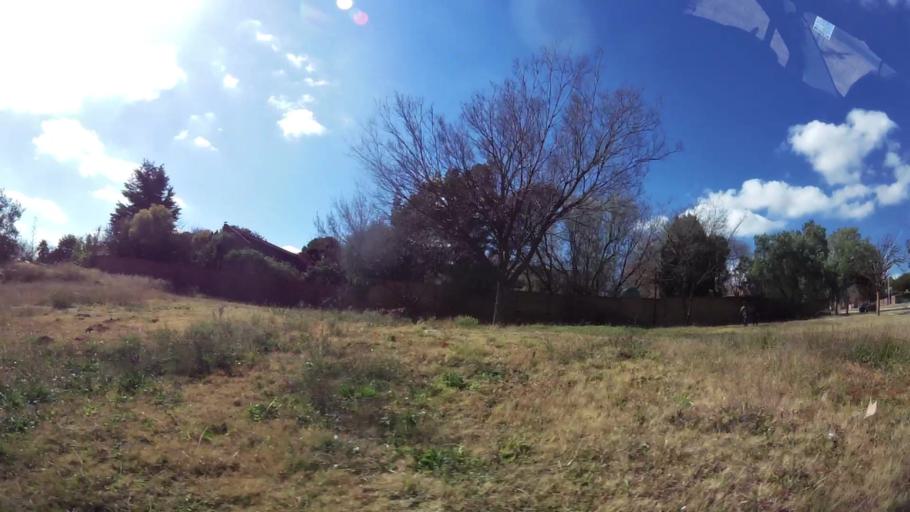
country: ZA
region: Gauteng
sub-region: West Rand District Municipality
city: Krugersdorp
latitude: -26.0967
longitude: 27.8010
